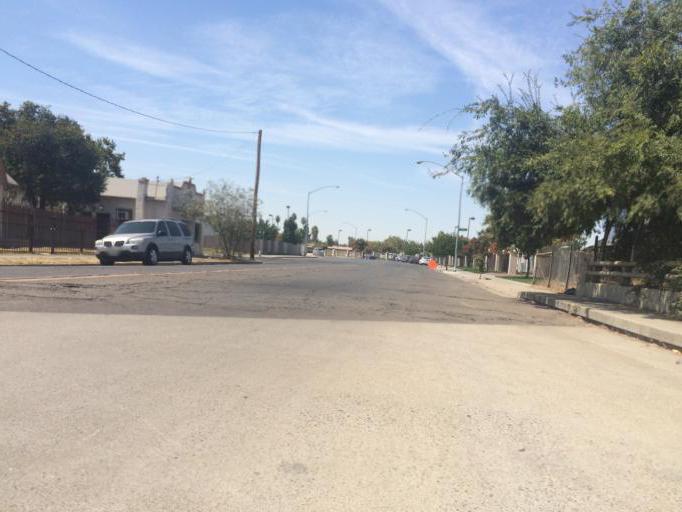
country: US
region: California
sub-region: Fresno County
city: Fresno
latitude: 36.7215
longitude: -119.7891
